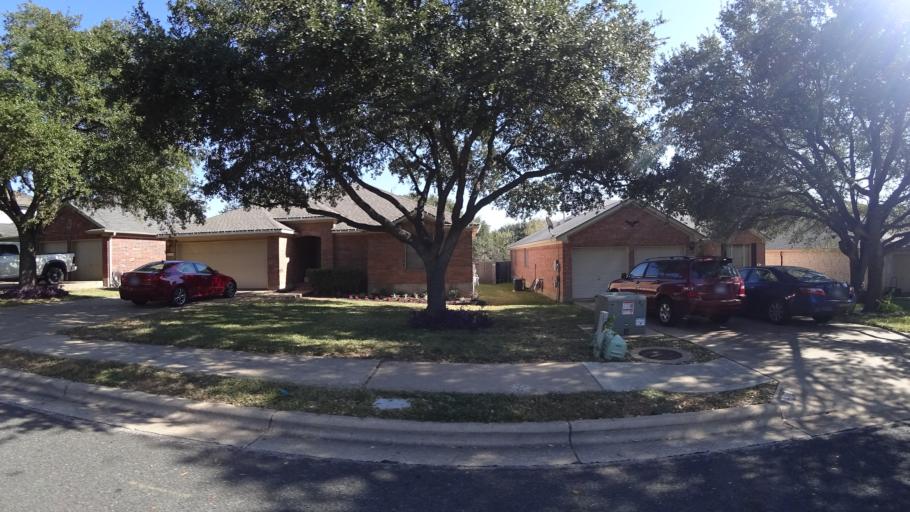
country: US
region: Texas
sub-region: Travis County
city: Shady Hollow
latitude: 30.2203
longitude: -97.8611
